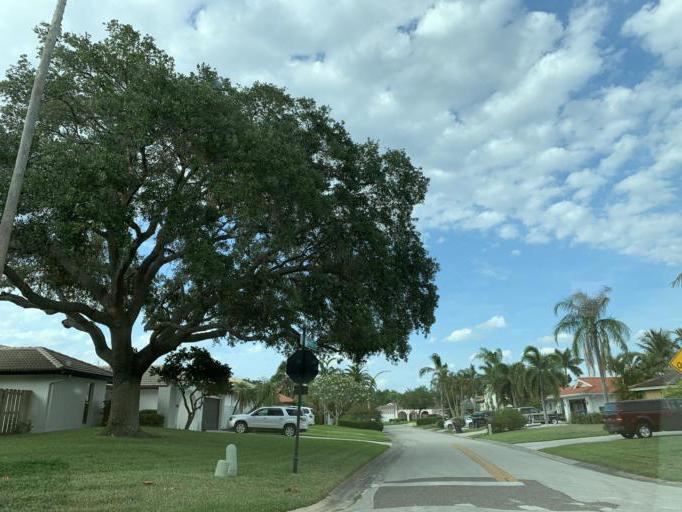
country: US
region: Florida
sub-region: Pinellas County
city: Gandy
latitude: 27.8182
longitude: -82.5961
